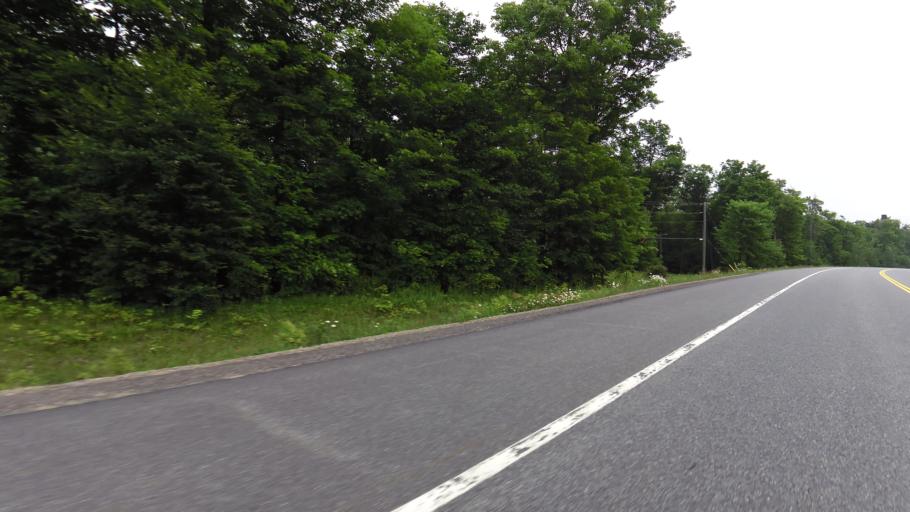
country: CA
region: Ontario
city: Huntsville
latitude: 45.4402
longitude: -78.8221
